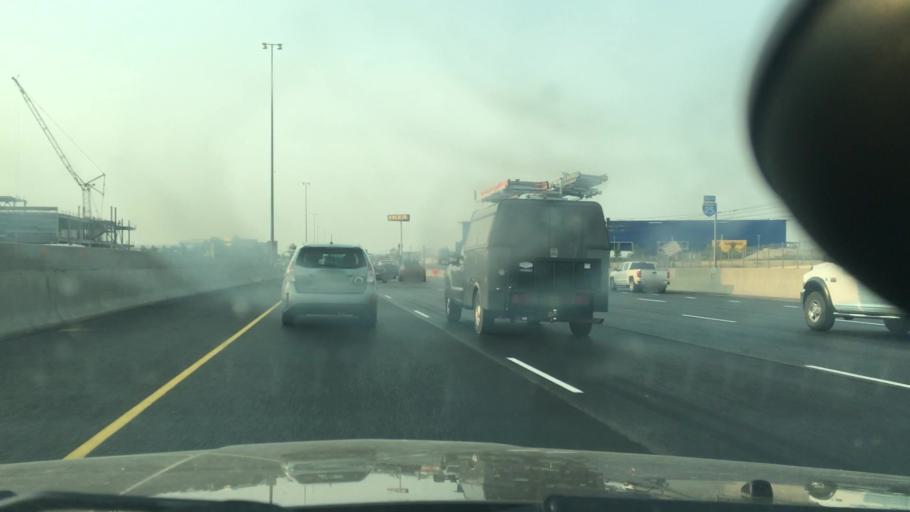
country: US
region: Colorado
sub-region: Arapahoe County
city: Centennial
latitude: 39.5764
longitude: -104.8754
